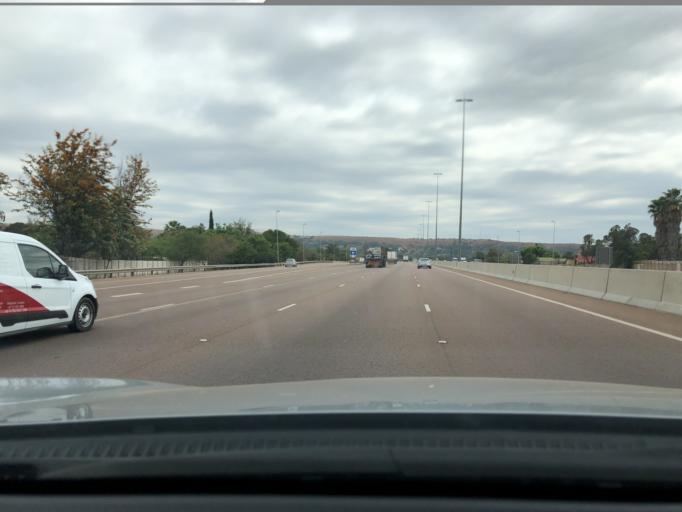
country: ZA
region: Gauteng
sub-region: City of Tshwane Metropolitan Municipality
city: Pretoria
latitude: -25.7182
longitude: 28.2654
